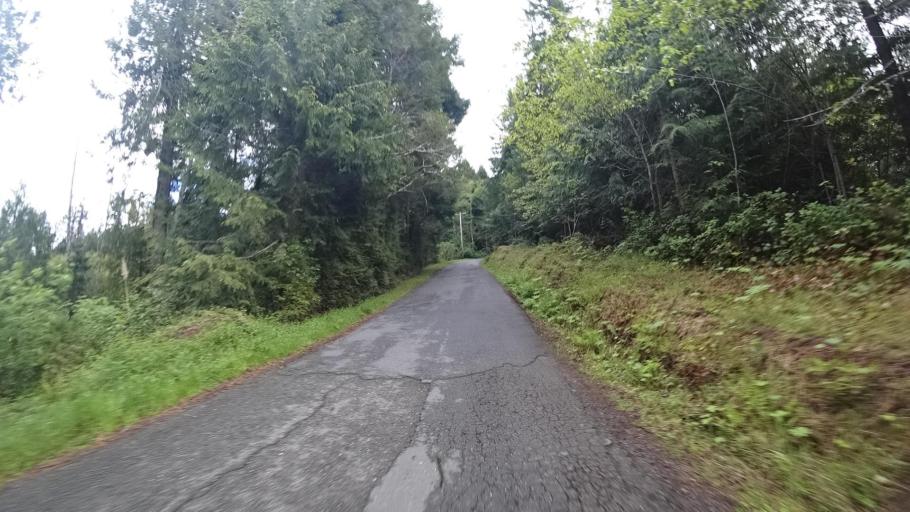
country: US
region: California
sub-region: Humboldt County
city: Bayside
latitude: 40.8257
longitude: -124.0085
